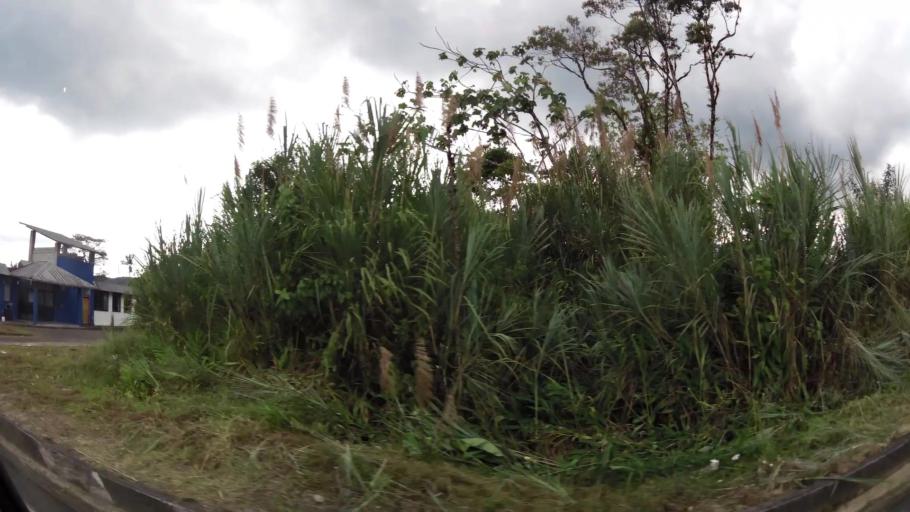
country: EC
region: Pastaza
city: Puyo
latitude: -1.4645
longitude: -78.1101
